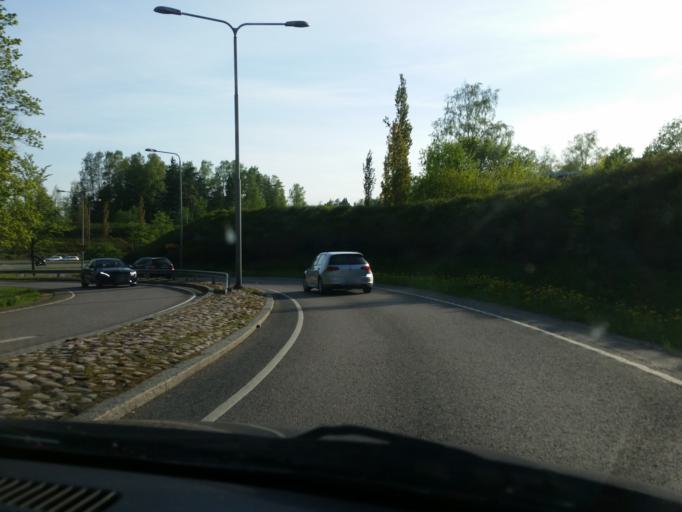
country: FI
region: Uusimaa
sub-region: Helsinki
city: Helsinki
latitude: 60.2420
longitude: 24.9254
